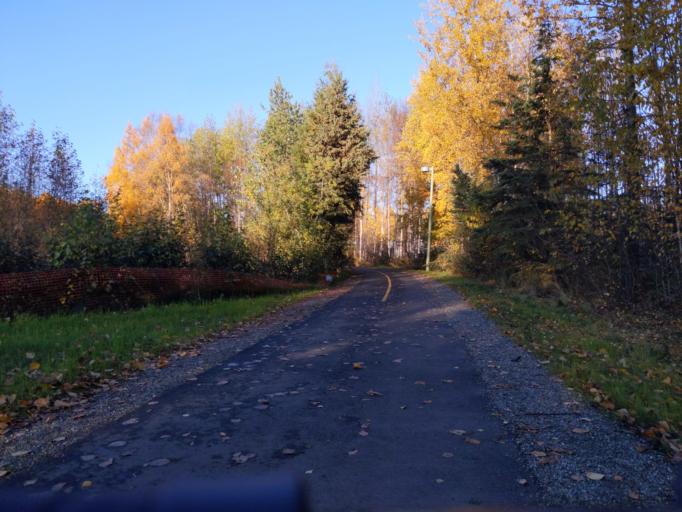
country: US
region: Alaska
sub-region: Anchorage Municipality
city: Anchorage
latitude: 61.1531
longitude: -149.8790
